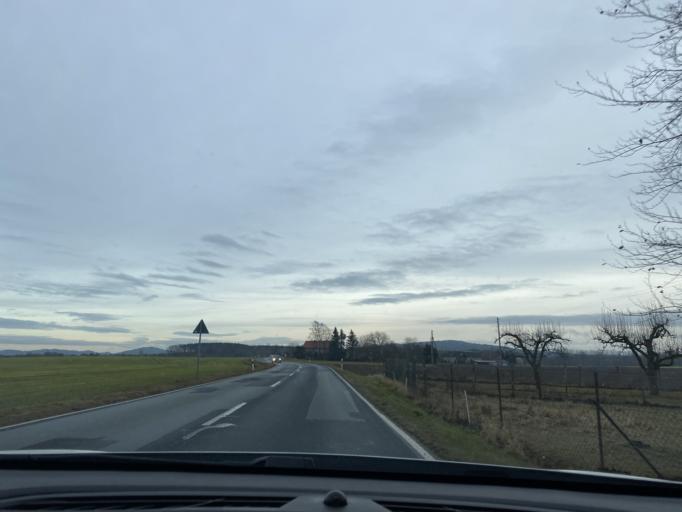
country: DE
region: Saxony
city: Reichenbach
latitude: 51.1216
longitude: 14.8251
